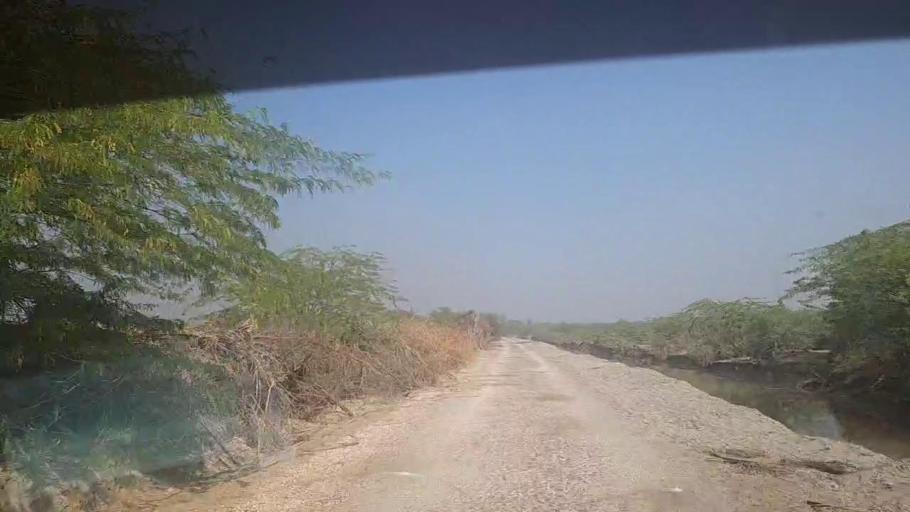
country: PK
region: Sindh
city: Khairpur
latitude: 27.4538
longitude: 68.7230
